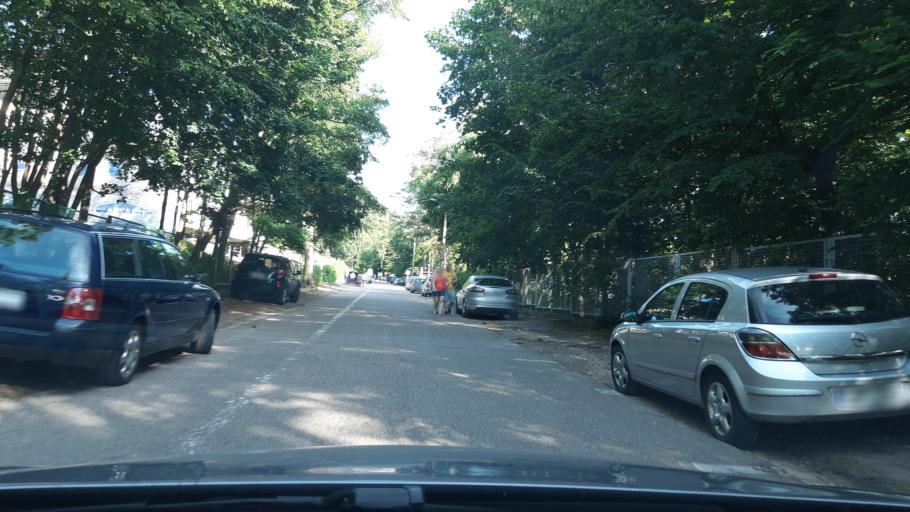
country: PL
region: Warmian-Masurian Voivodeship
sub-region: Powiat mragowski
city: Mragowo
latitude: 53.8744
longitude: 21.3197
